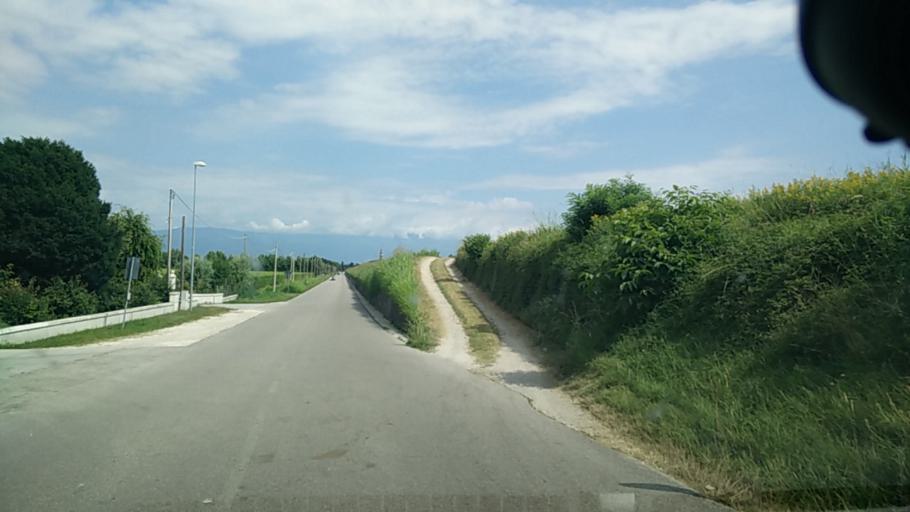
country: IT
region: Friuli Venezia Giulia
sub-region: Provincia di Pordenone
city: Puia-Villanova
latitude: 45.8290
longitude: 12.5701
